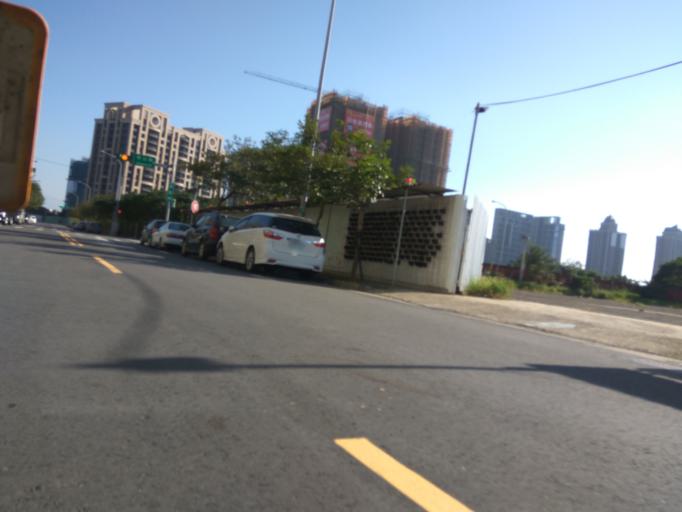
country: TW
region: Taiwan
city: Taoyuan City
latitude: 25.0142
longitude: 121.2199
